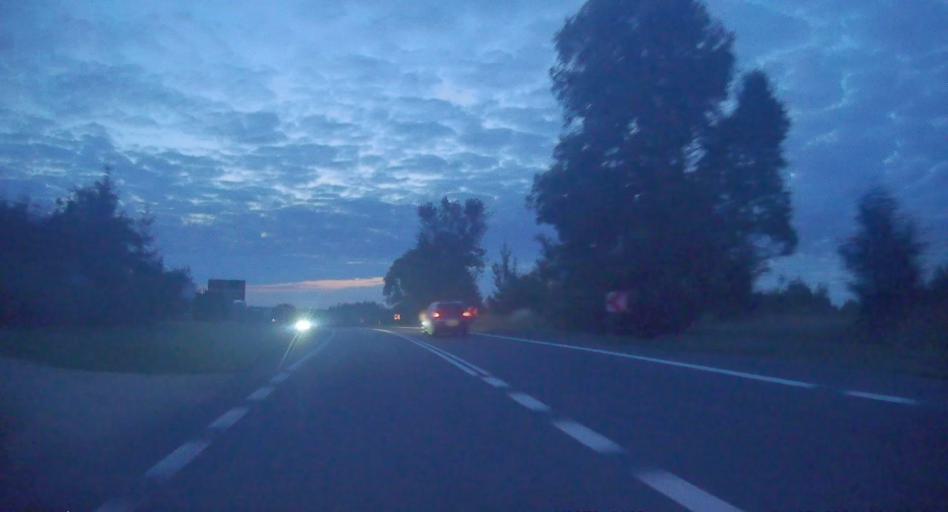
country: PL
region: Silesian Voivodeship
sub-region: Powiat klobucki
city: Kamyk
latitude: 50.8807
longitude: 18.9938
